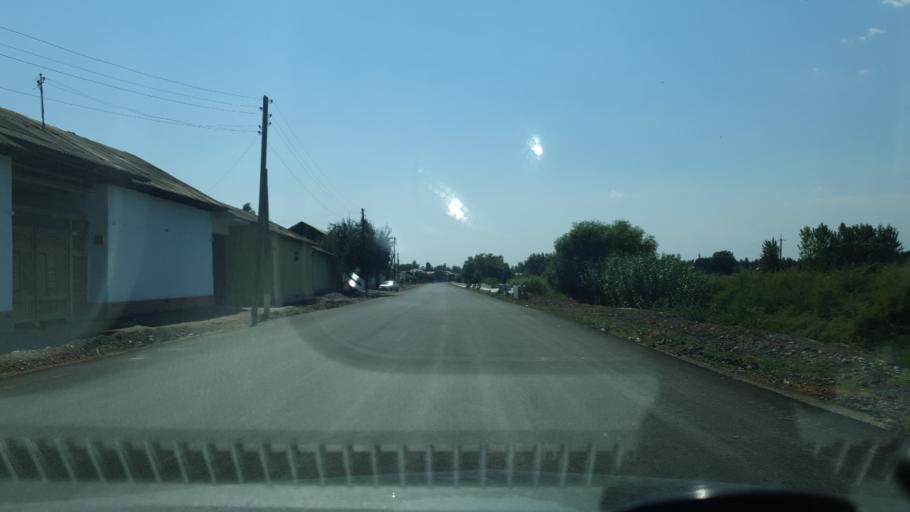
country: UZ
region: Namangan
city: Pop
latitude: 40.6355
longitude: 71.1980
